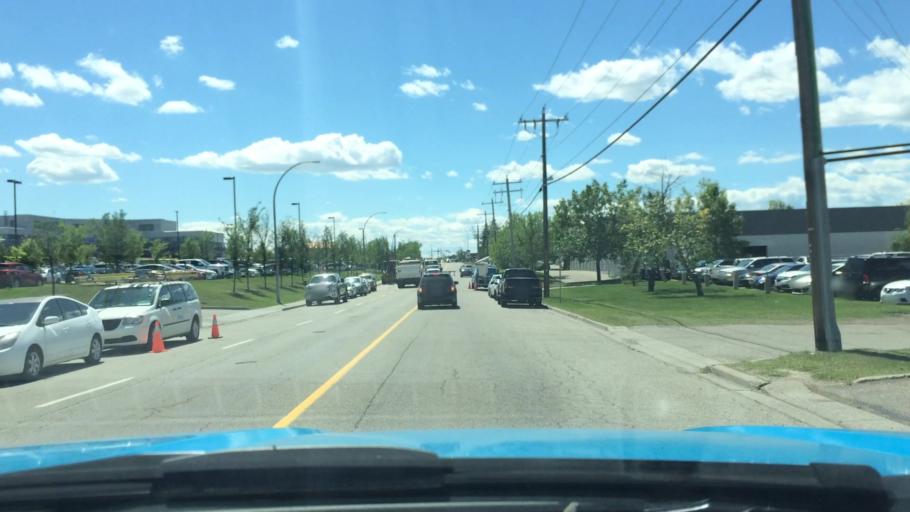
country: CA
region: Alberta
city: Calgary
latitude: 51.0854
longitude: -114.0051
